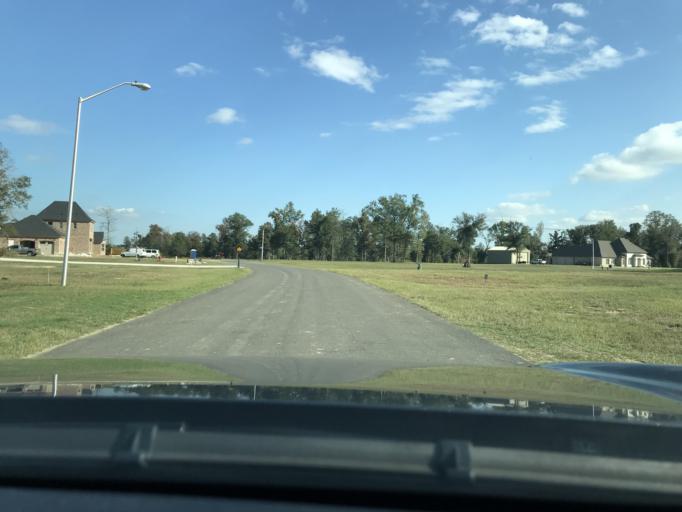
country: US
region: Louisiana
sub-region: Calcasieu Parish
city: Moss Bluff
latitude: 30.3341
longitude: -93.2490
